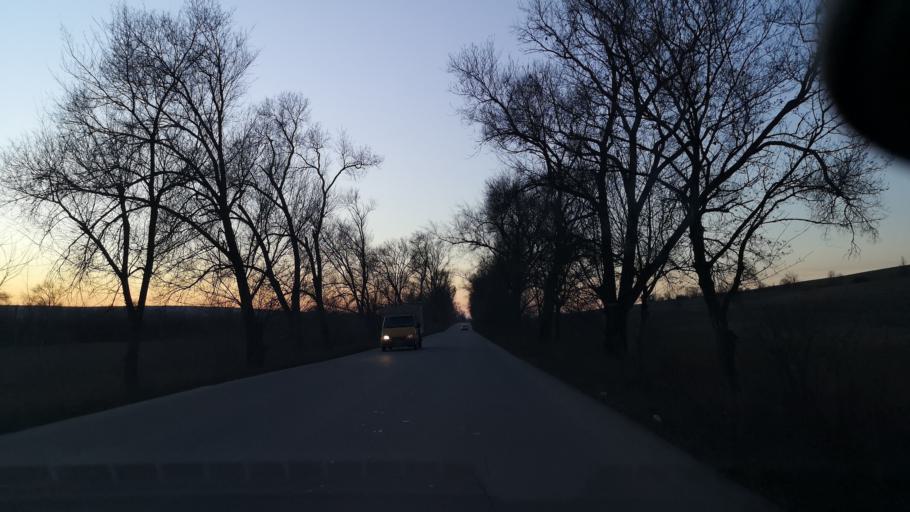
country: MD
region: Anenii Noi
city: Anenii Noi
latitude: 46.8884
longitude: 29.2591
